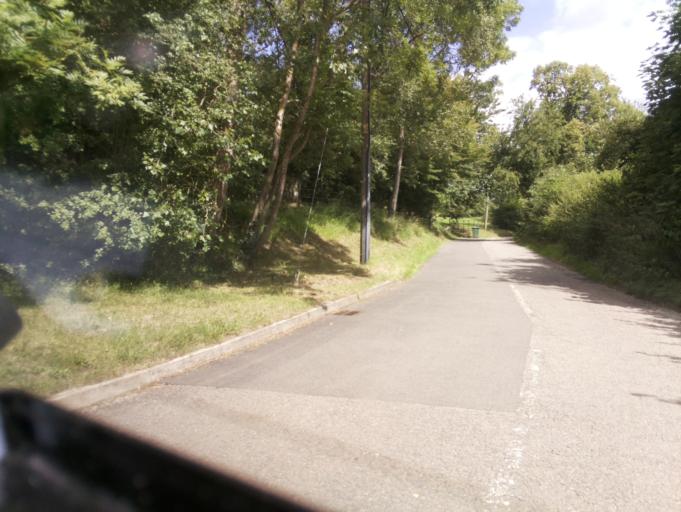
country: GB
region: England
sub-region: Buckinghamshire
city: Winslow
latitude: 51.9348
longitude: -0.8345
